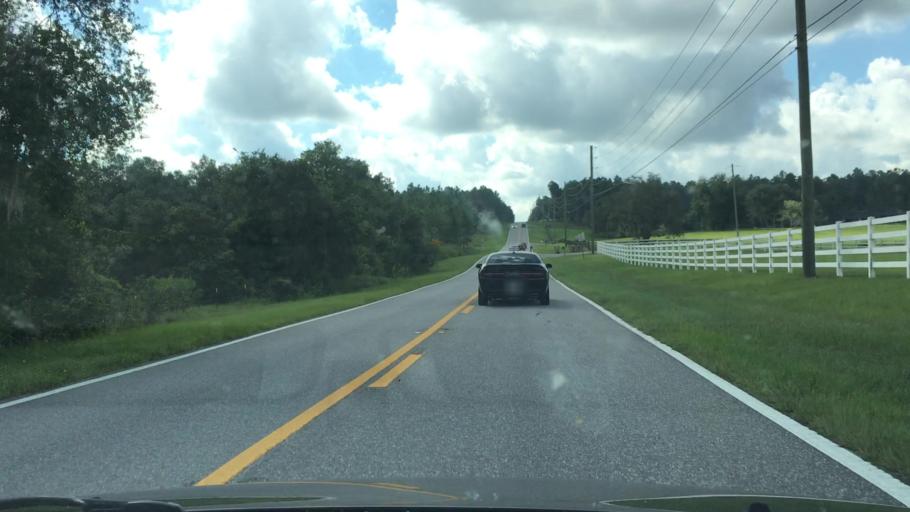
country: US
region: Florida
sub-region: Lake County
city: Astatula
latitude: 28.6627
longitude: -81.7293
